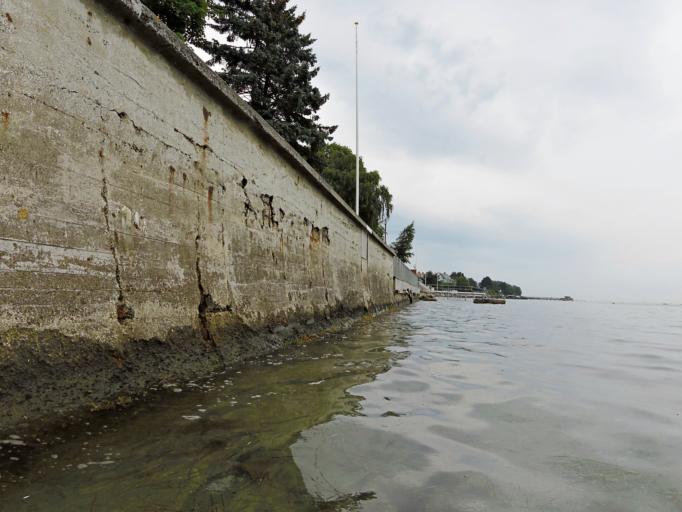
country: DK
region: Capital Region
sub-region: Gentofte Kommune
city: Charlottenlund
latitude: 55.7377
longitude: 12.5834
